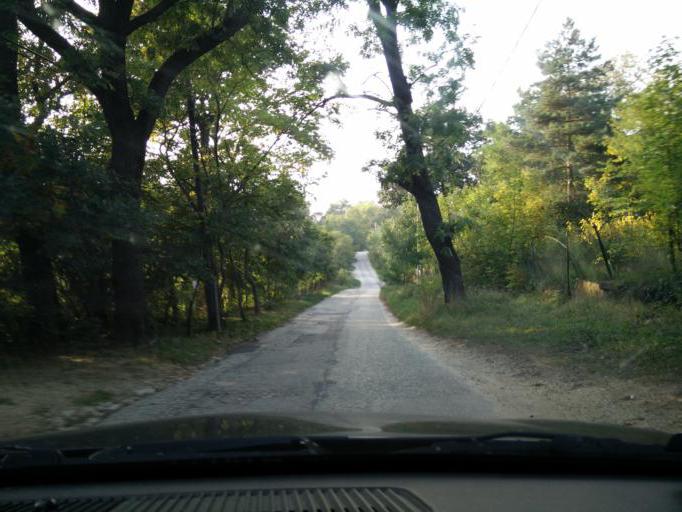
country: HU
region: Pest
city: Piliscsaba
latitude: 47.6434
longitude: 18.8279
